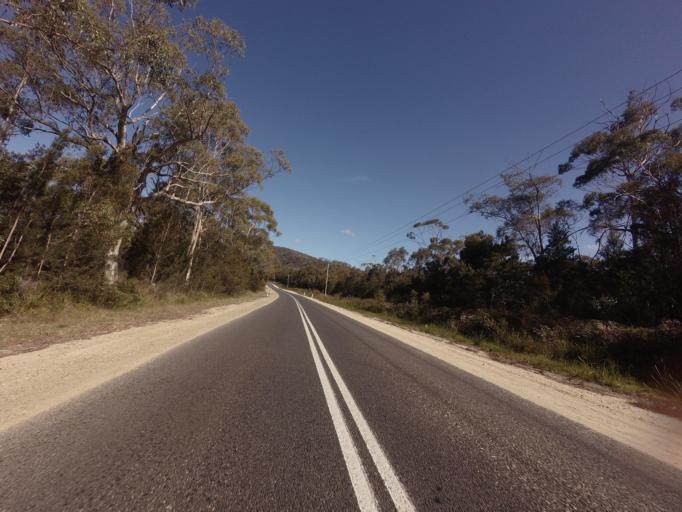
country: AU
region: Tasmania
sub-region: Break O'Day
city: St Helens
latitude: -41.8429
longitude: 148.2546
